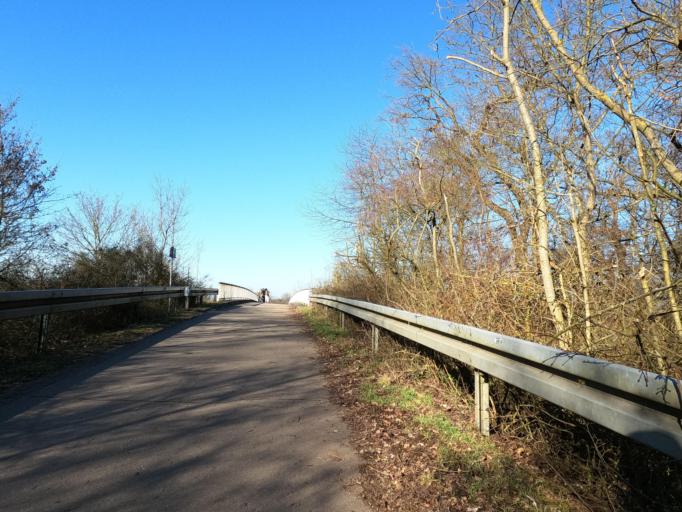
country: DE
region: Hesse
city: Kelsterbach
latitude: 50.0806
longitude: 8.5601
